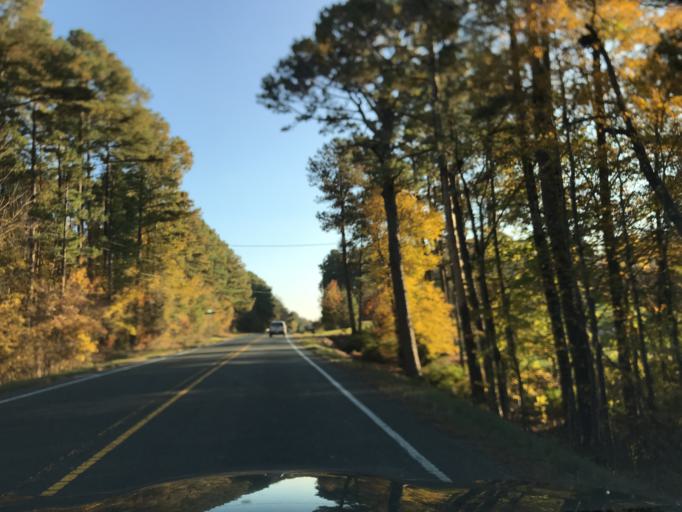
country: US
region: North Carolina
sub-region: Granville County
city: Creedmoor
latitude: 36.0088
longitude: -78.6876
